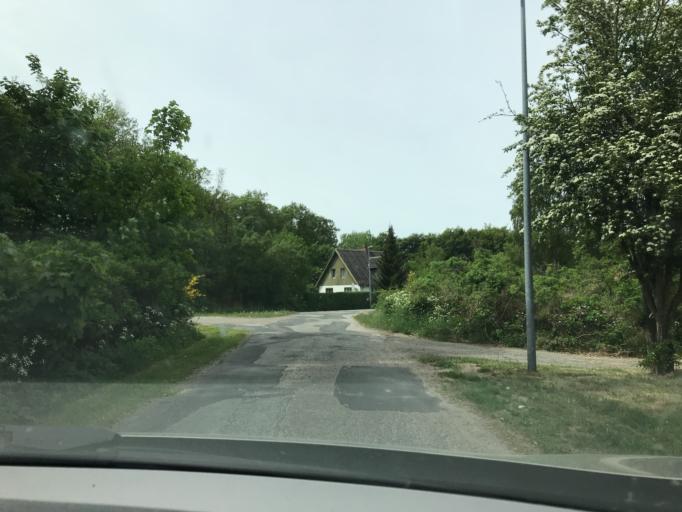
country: DK
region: Central Jutland
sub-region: Norddjurs Kommune
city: Allingabro
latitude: 56.5985
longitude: 10.3128
